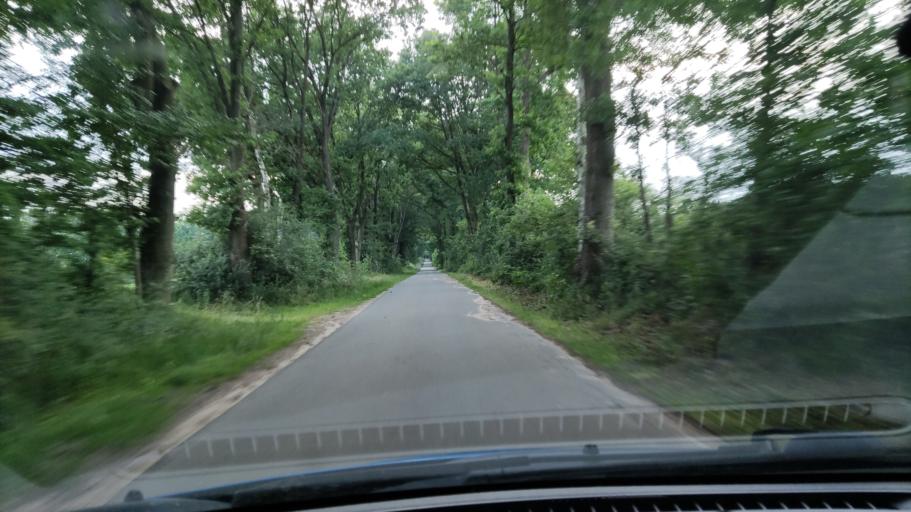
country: DE
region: Lower Saxony
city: Amelinghausen
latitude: 53.1327
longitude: 10.2435
